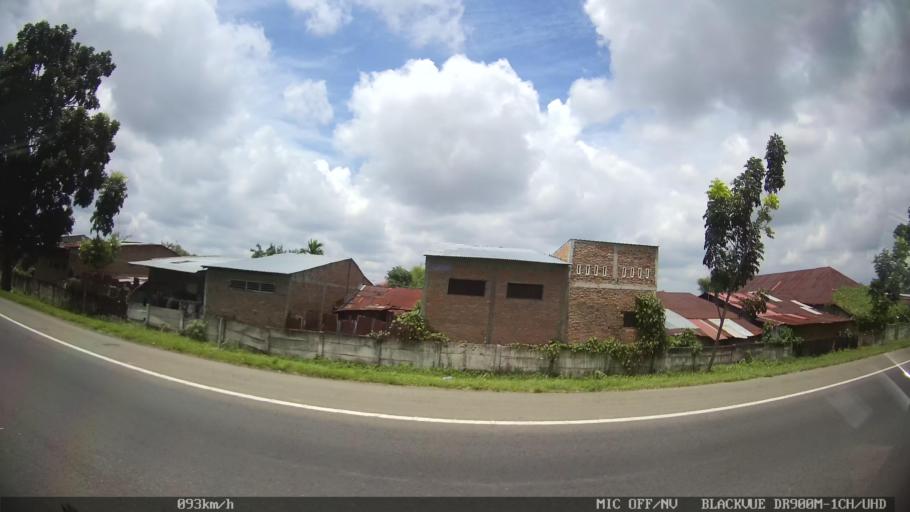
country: ID
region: North Sumatra
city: Medan
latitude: 3.6110
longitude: 98.7218
